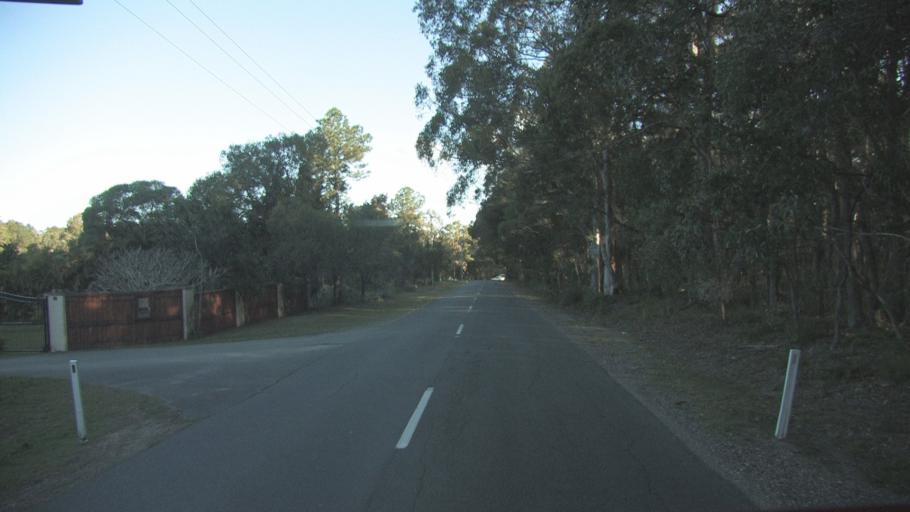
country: AU
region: Queensland
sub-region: Gold Coast
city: Yatala
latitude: -27.6841
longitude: 153.2745
